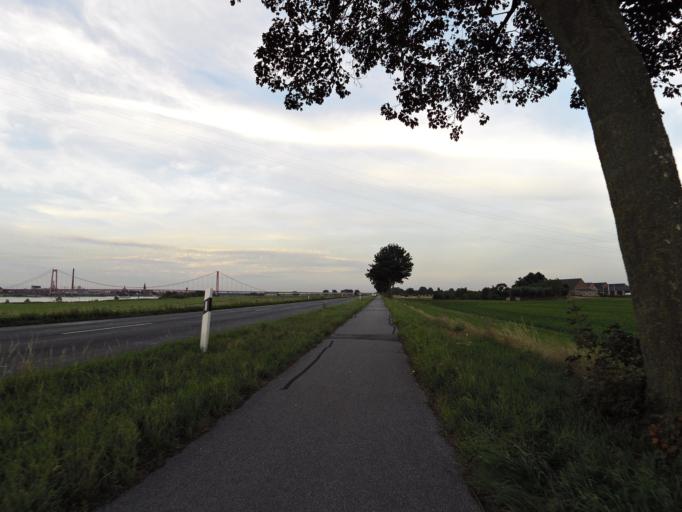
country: DE
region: North Rhine-Westphalia
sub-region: Regierungsbezirk Dusseldorf
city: Emmerich
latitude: 51.8256
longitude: 6.2097
